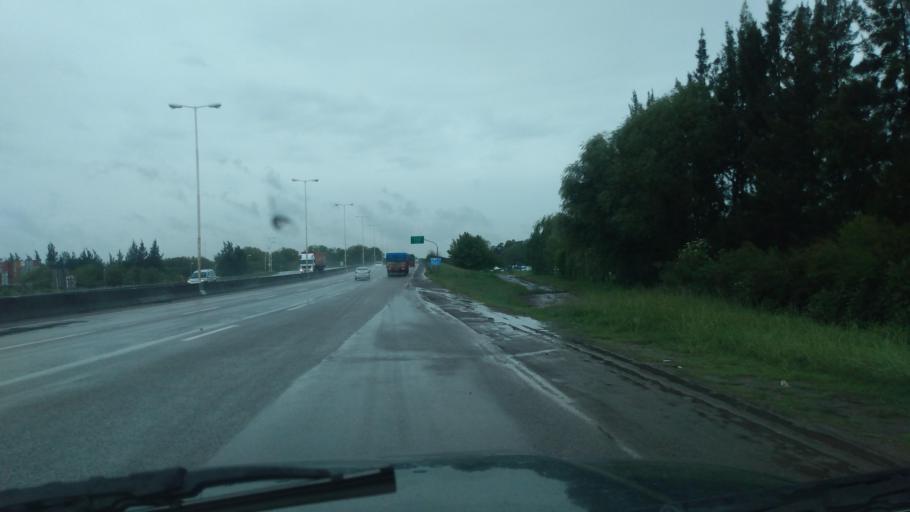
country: AR
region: Buenos Aires
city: Capilla del Senor
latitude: -34.3915
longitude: -59.0382
